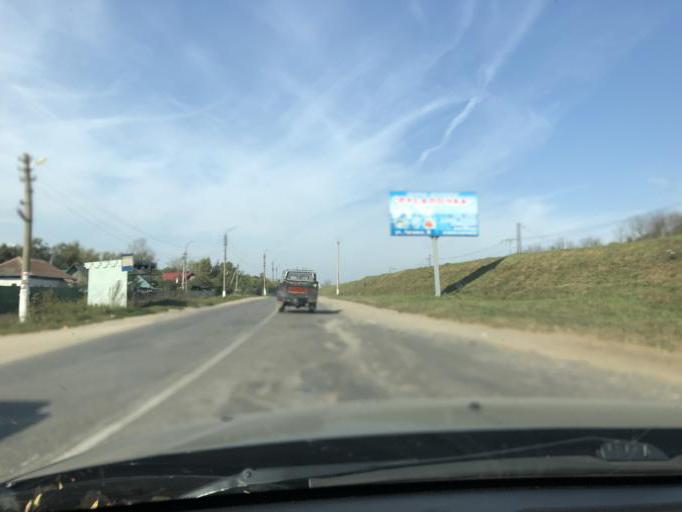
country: RU
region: Tula
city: Yasnogorsk
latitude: 54.4813
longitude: 37.6824
